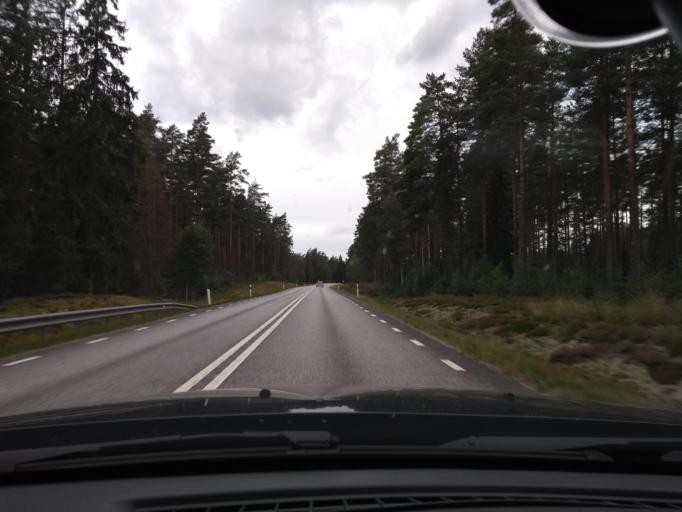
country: SE
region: OEstergoetland
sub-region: Ydre Kommun
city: OEsterbymo
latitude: 57.6416
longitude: 15.2193
